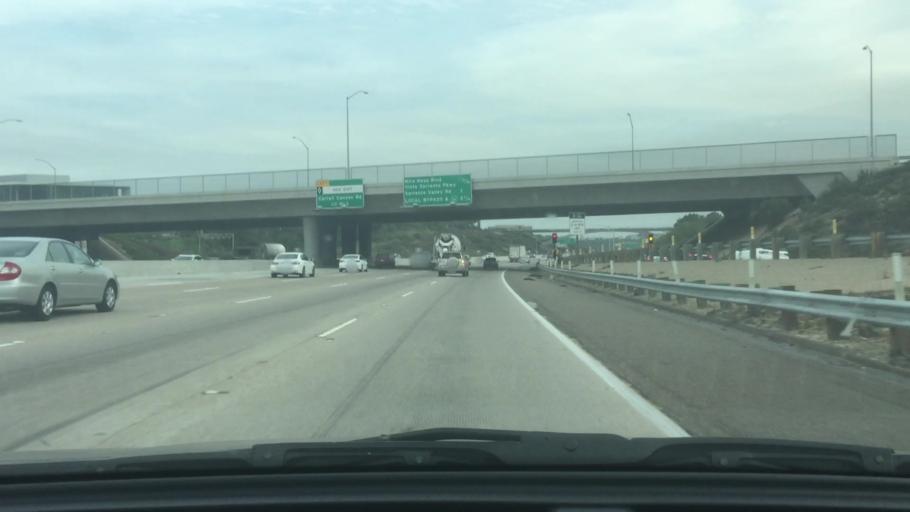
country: US
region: California
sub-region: San Diego County
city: La Jolla
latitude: 32.8744
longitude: -117.1986
